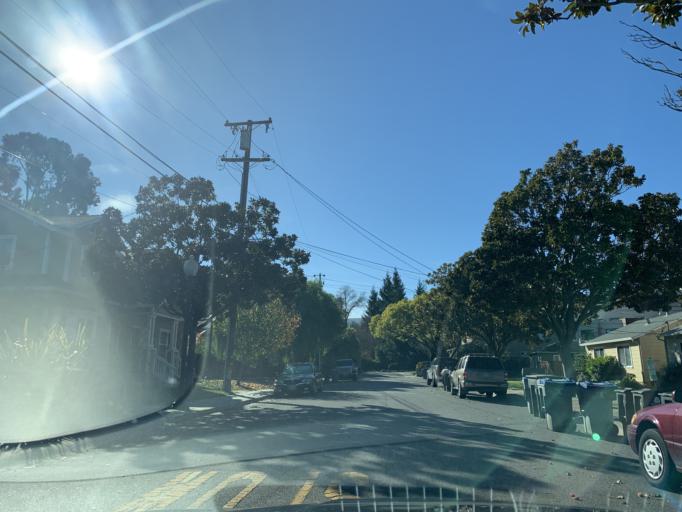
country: US
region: California
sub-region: Santa Clara County
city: Mountain View
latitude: 37.3923
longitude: -122.0929
